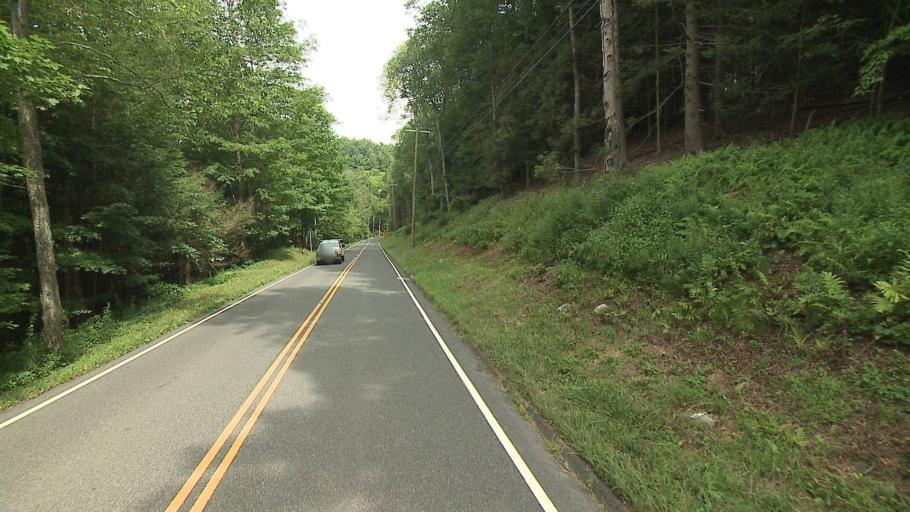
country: US
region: Connecticut
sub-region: Litchfield County
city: New Milford
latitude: 41.5902
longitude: -73.3217
